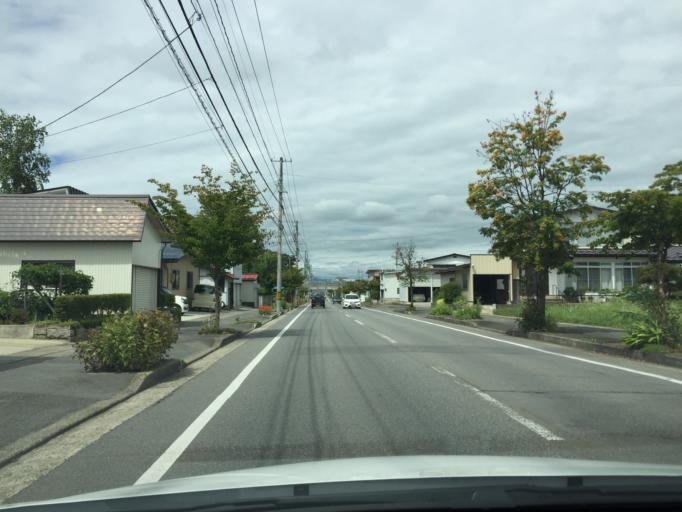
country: JP
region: Yamagata
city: Yonezawa
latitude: 37.8954
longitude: 140.1254
